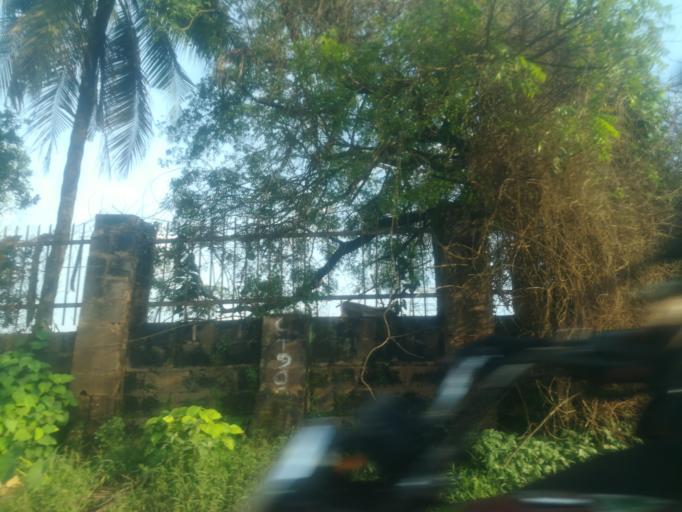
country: NG
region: Oyo
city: Ibadan
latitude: 7.3780
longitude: 3.8131
